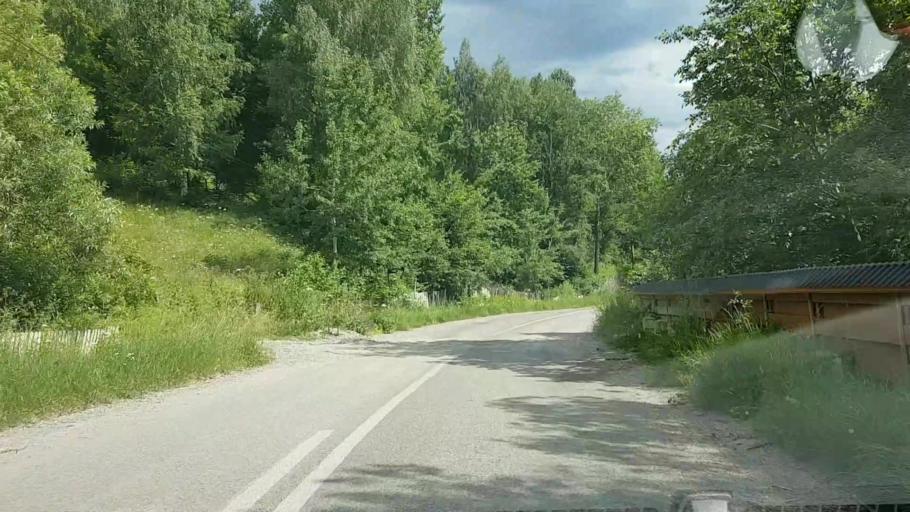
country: RO
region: Neamt
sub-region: Comuna Ceahlau
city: Ceahlau
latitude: 47.0658
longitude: 25.9620
